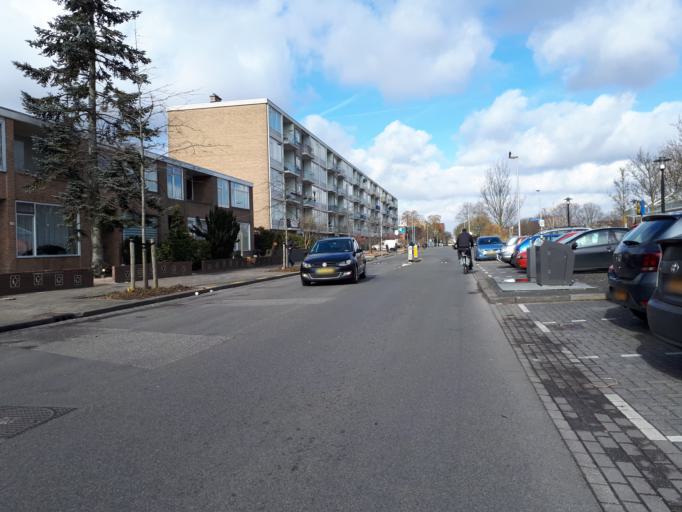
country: NL
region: Utrecht
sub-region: Gemeente Utrecht
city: Utrecht
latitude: 52.0659
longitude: 5.0977
